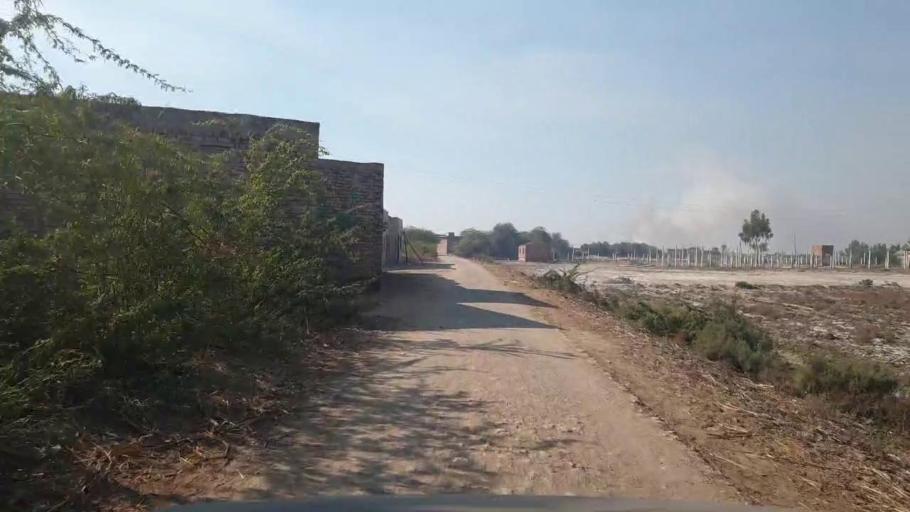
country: PK
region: Sindh
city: Mirwah Gorchani
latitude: 25.3033
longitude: 69.0944
